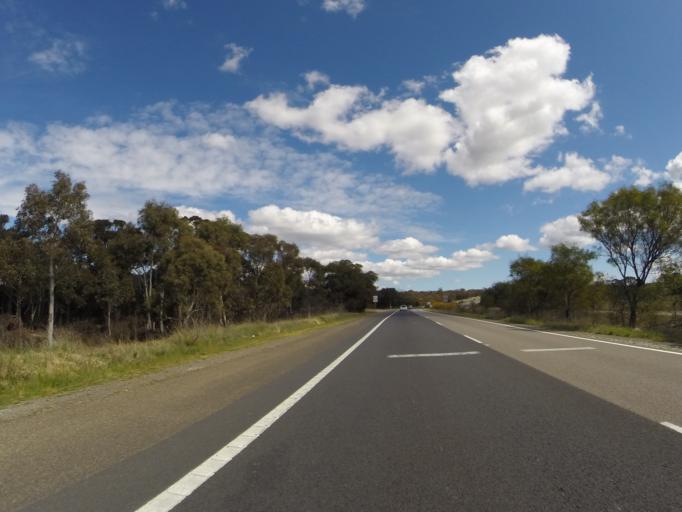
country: AU
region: New South Wales
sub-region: Goulburn Mulwaree
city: Goulburn
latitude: -34.7337
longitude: 149.9718
